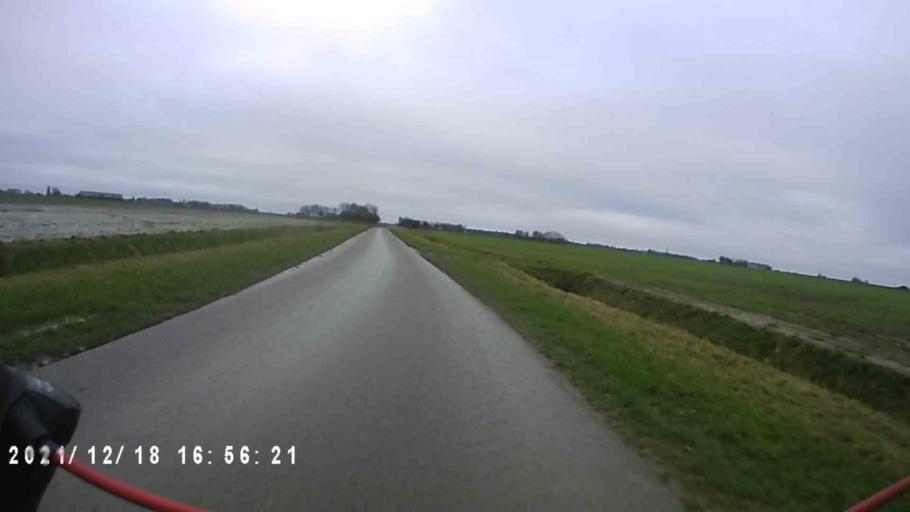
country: NL
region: Friesland
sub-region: Gemeente Dongeradeel
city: Ternaard
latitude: 53.3701
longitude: 5.9421
